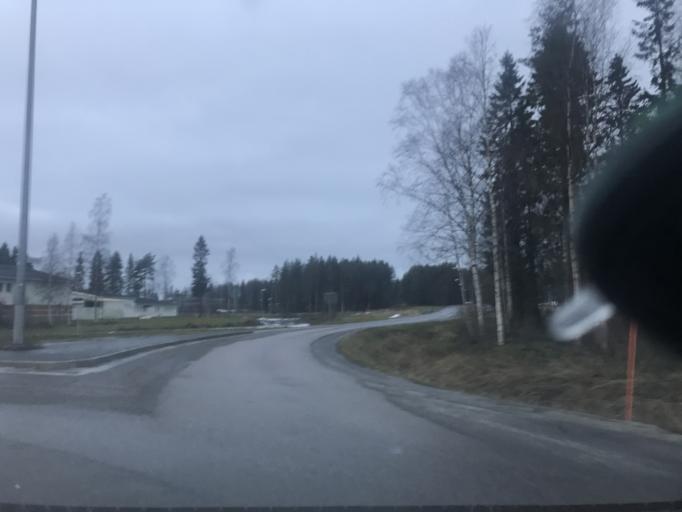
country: SE
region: Norrbotten
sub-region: Lulea Kommun
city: Bergnaset
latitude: 65.6153
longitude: 22.1233
